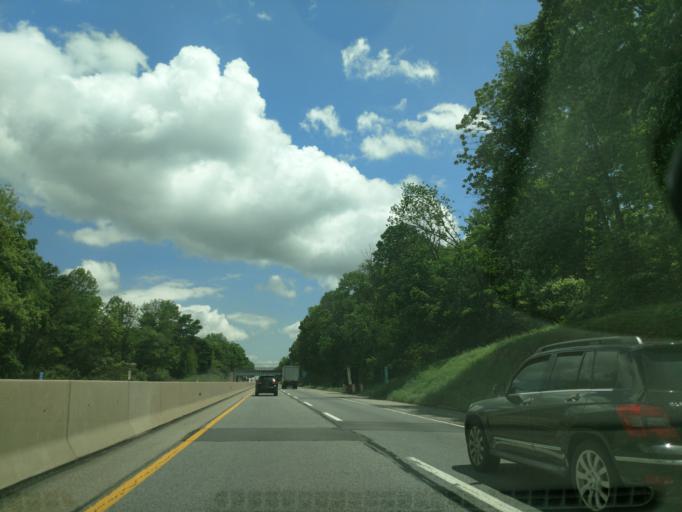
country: US
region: Pennsylvania
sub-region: Lancaster County
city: Swartzville
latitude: 40.2136
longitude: -76.0610
